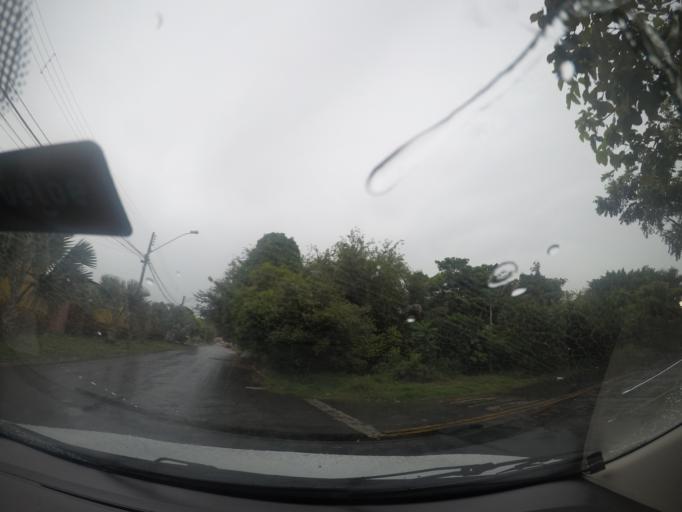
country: BR
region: Goias
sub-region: Goiania
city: Goiania
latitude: -16.6473
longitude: -49.2251
